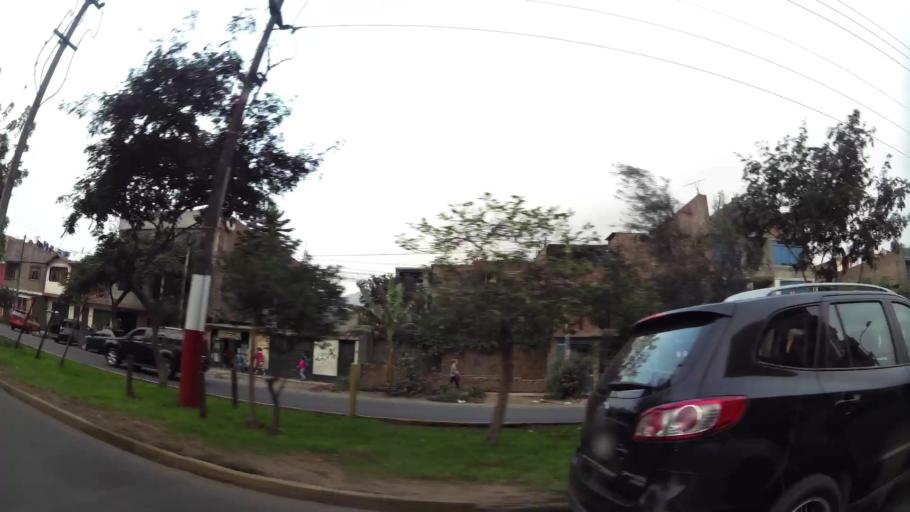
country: PE
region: Lima
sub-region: Lima
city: Independencia
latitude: -11.9973
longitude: -77.0052
